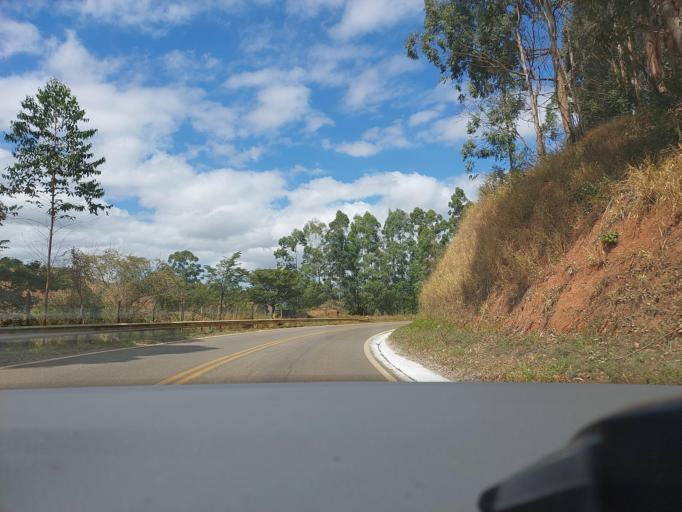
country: BR
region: Minas Gerais
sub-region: Visconde Do Rio Branco
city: Visconde do Rio Branco
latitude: -20.9181
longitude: -42.6386
